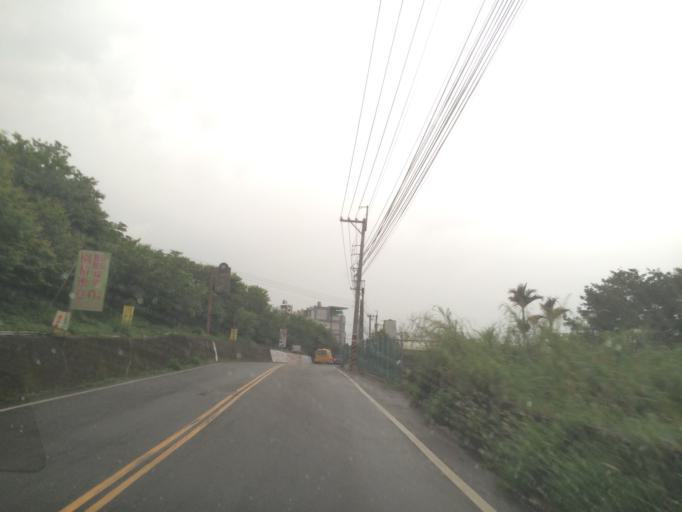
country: TW
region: Taiwan
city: Fengyuan
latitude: 24.1837
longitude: 120.8158
